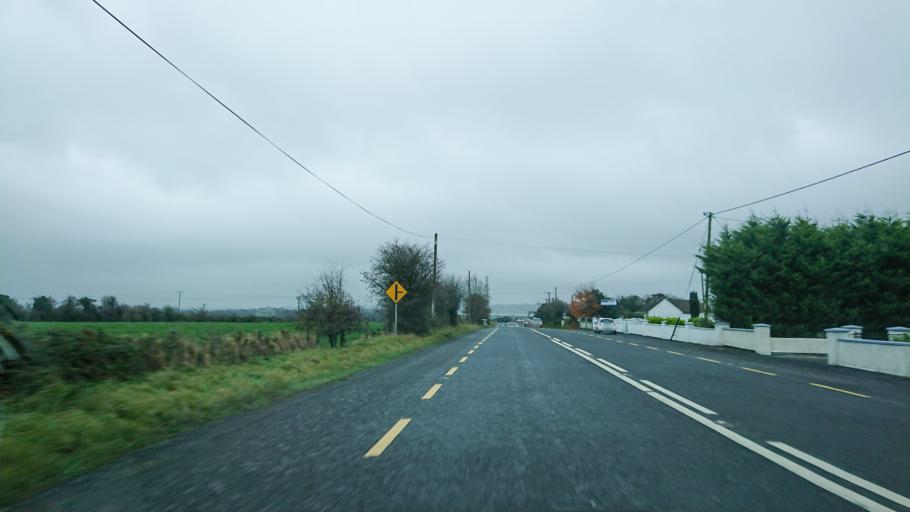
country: IE
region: Munster
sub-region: Waterford
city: Waterford
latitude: 52.2813
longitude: -7.1733
